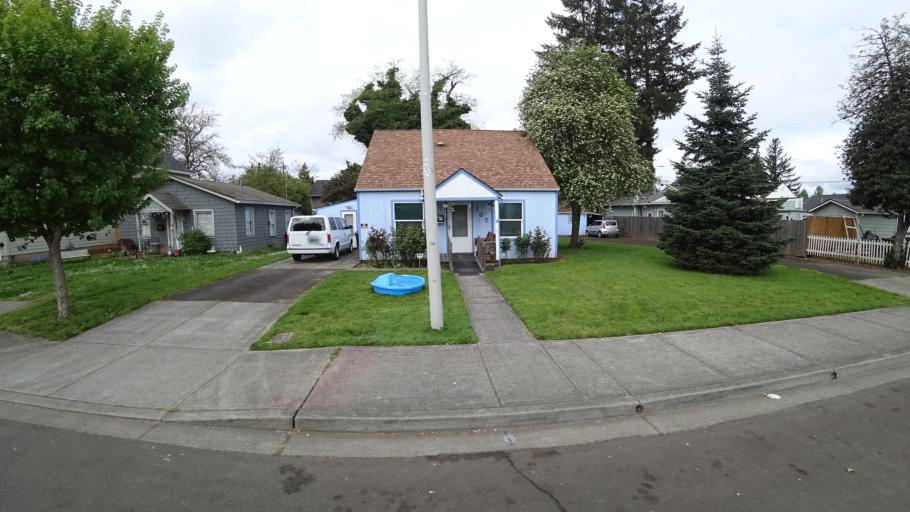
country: US
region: Oregon
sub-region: Washington County
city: Hillsboro
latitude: 45.5236
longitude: -122.9929
